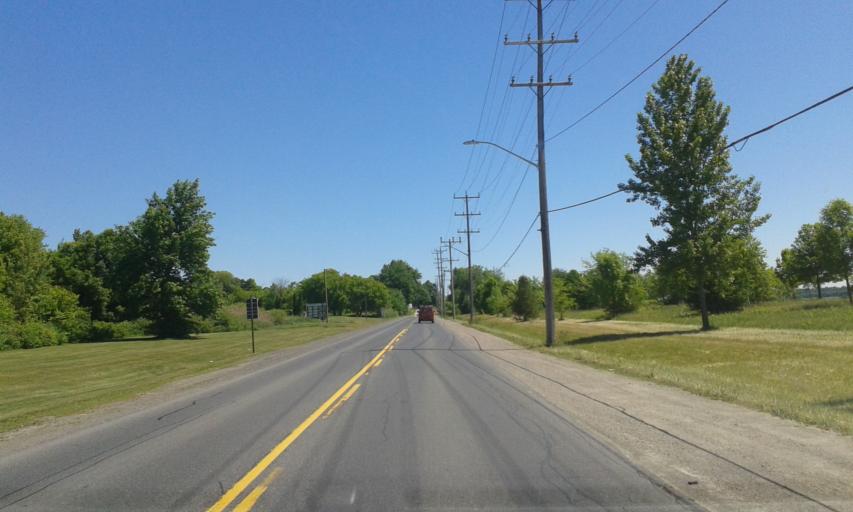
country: CA
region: Ontario
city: Prescott
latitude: 44.7136
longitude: -75.5053
